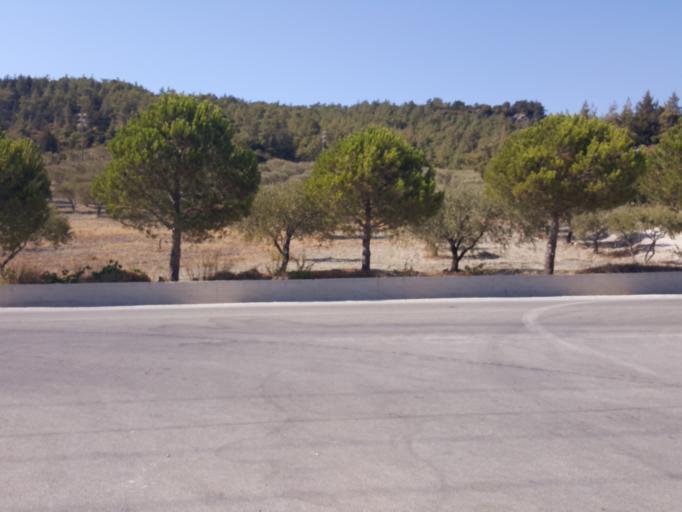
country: GR
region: South Aegean
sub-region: Nomos Dodekanisou
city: Emponas
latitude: 36.2382
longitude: 27.8721
